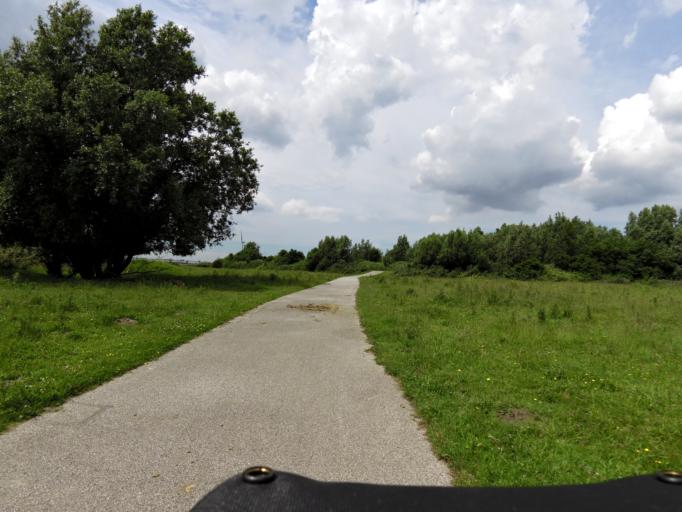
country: NL
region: South Holland
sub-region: Gemeente Westland
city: Maasdijk
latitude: 51.9321
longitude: 4.2034
